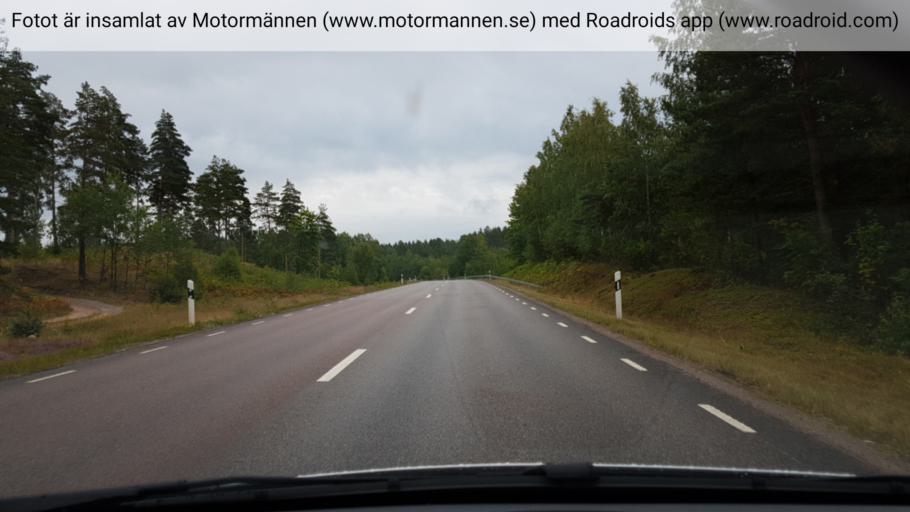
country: SE
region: Vaestra Goetaland
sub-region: Tibro Kommun
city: Tibro
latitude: 58.4543
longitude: 14.2520
